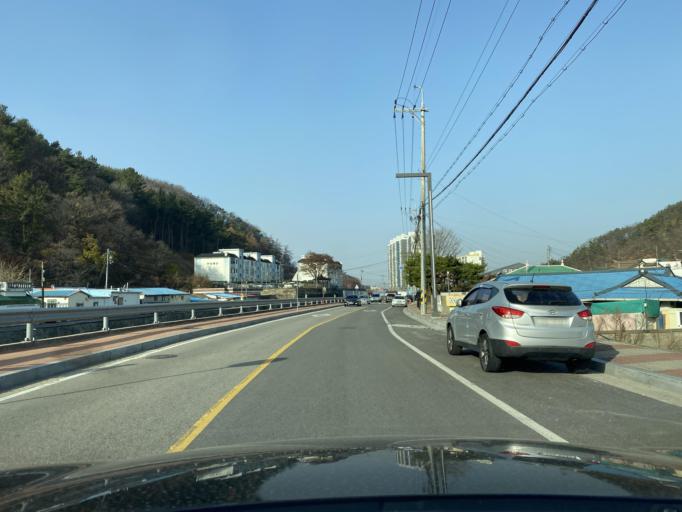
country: KR
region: Chungcheongnam-do
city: Yesan
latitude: 36.6766
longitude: 126.8427
